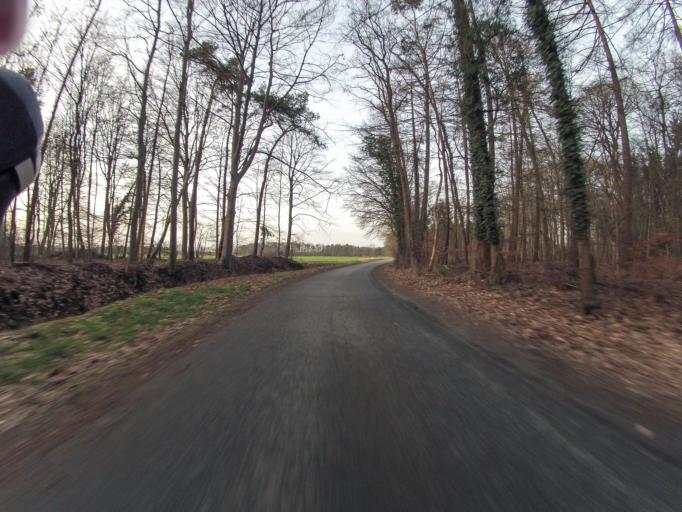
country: DE
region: North Rhine-Westphalia
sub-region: Regierungsbezirk Munster
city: Steinfurt
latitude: 52.1774
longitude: 7.3318
